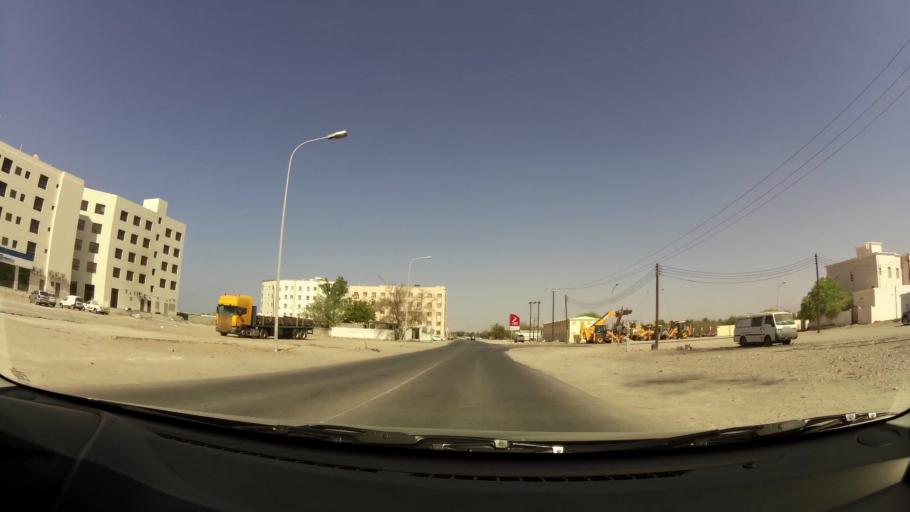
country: OM
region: Muhafazat Masqat
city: As Sib al Jadidah
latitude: 23.6101
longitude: 58.2419
